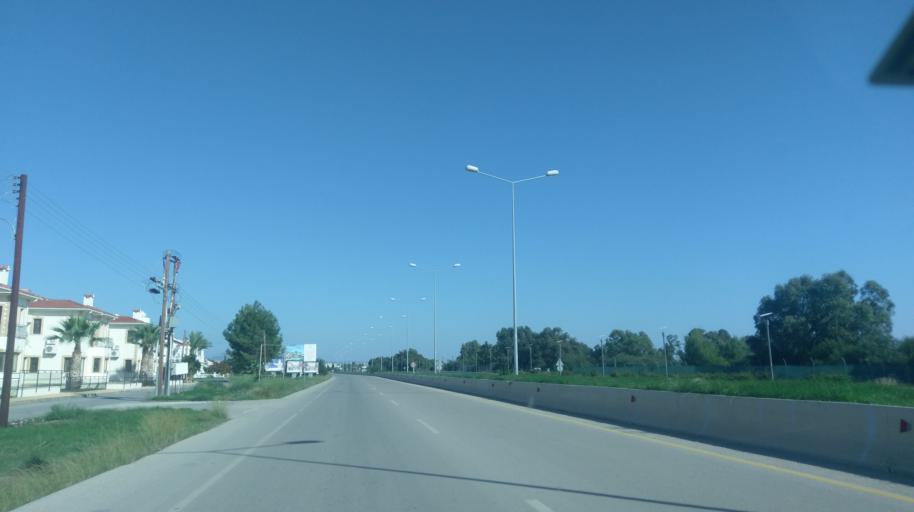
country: CY
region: Ammochostos
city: Trikomo
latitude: 35.2690
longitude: 33.9145
